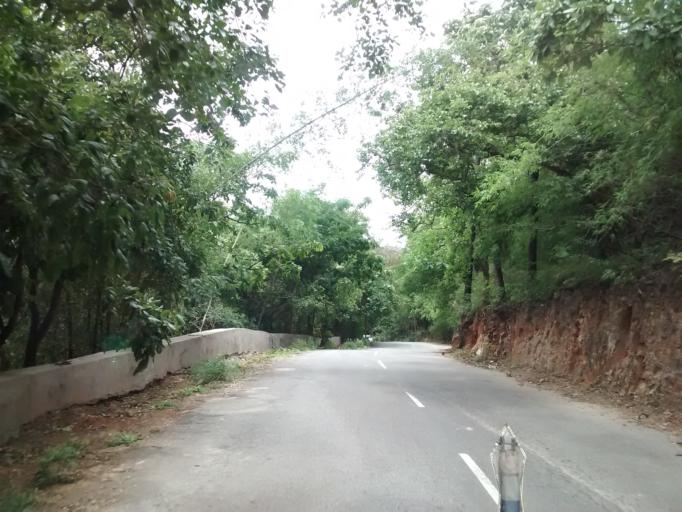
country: IN
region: Andhra Pradesh
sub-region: Chittoor
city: Tirumala
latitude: 13.6786
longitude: 79.3314
